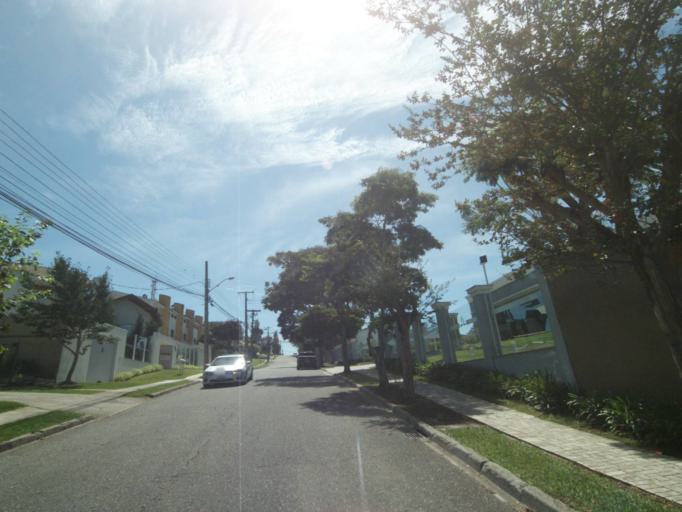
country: BR
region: Parana
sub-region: Curitiba
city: Curitiba
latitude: -25.4618
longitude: -49.2401
